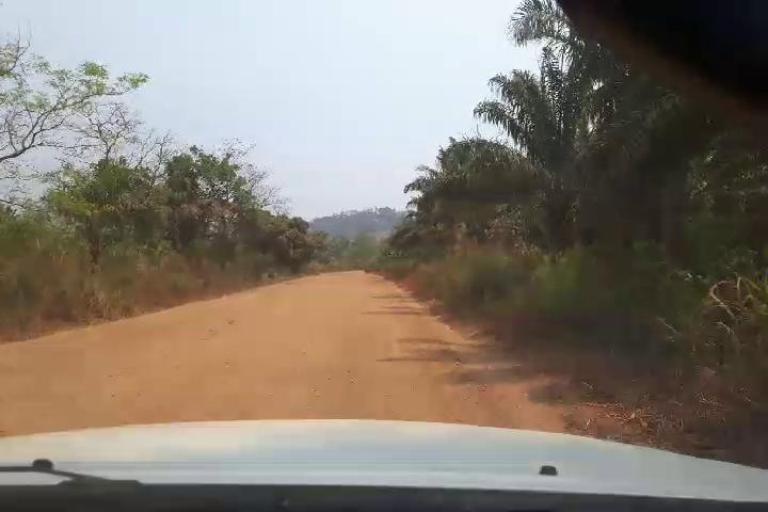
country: SL
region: Northern Province
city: Bumbuna
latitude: 9.0195
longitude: -11.7645
